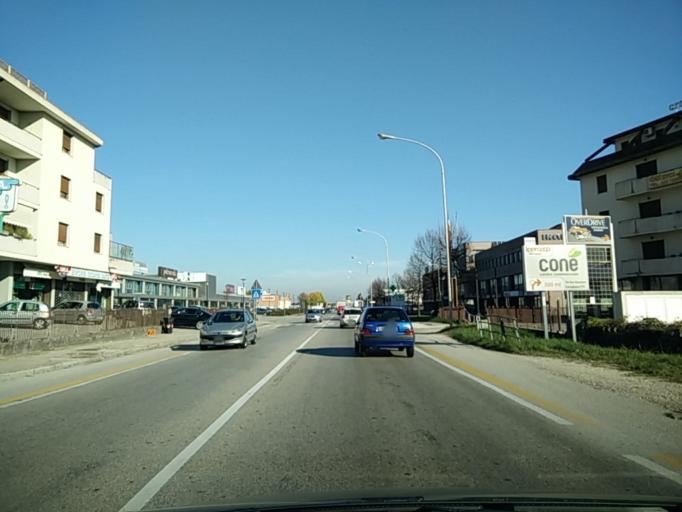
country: IT
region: Veneto
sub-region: Provincia di Treviso
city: Conegliano
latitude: 45.8781
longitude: 12.3054
